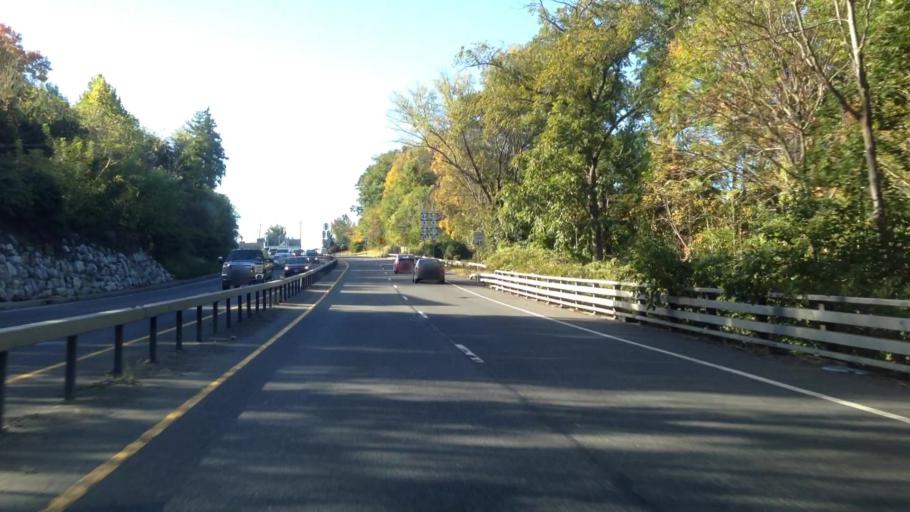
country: US
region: New York
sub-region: Ulster County
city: Highland
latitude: 41.7194
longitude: -73.9616
